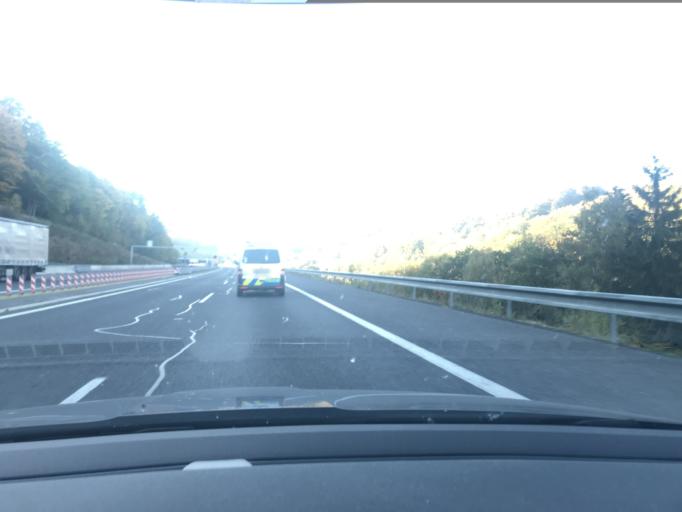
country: CZ
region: Ustecky
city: Libouchec
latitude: 50.7492
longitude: 14.0010
